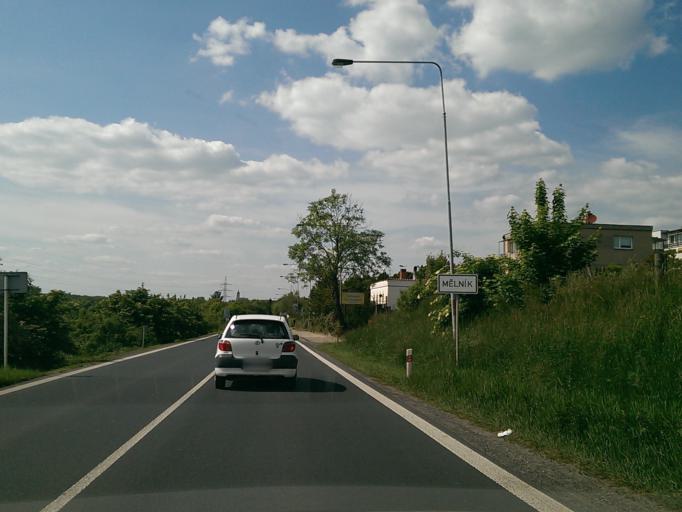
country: CZ
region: Central Bohemia
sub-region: Okres Melnik
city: Melnik
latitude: 50.3305
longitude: 14.4996
